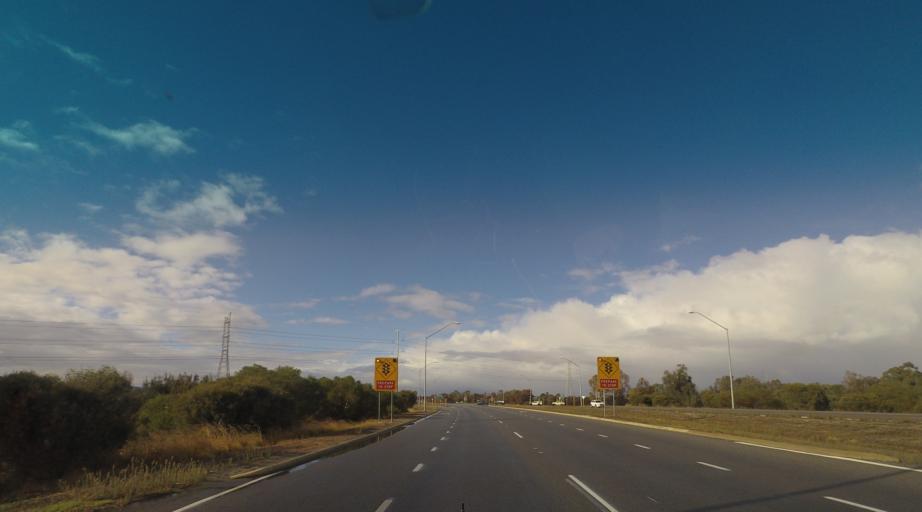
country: AU
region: Western Australia
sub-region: Armadale
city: Seville Grove
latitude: -32.1462
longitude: 115.9565
